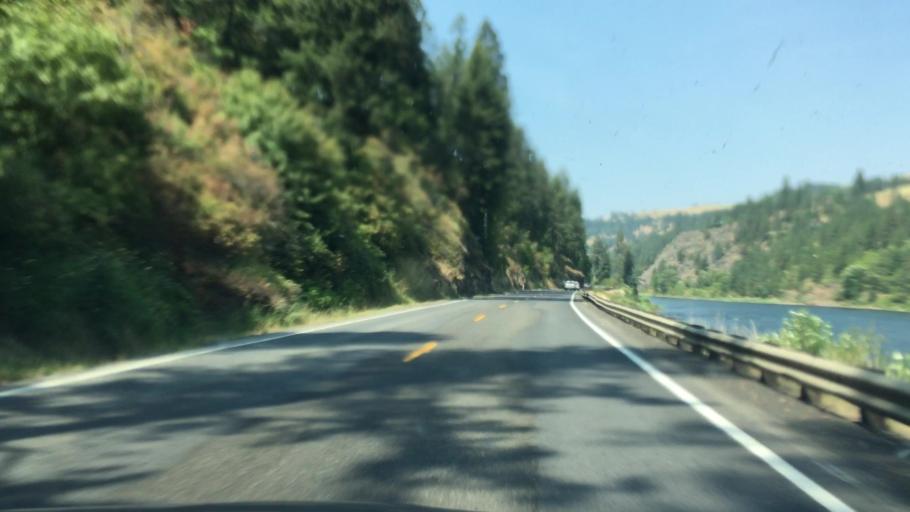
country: US
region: Idaho
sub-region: Clearwater County
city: Orofino
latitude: 46.4966
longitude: -116.4100
